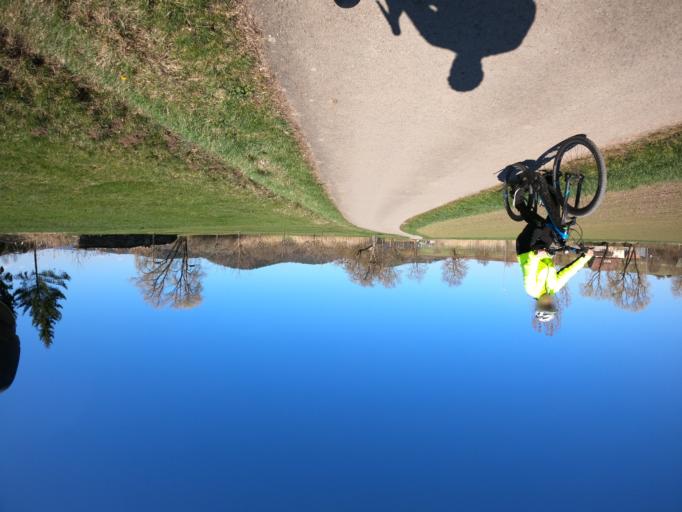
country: DE
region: Baden-Wuerttemberg
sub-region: Tuebingen Region
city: Rangendingen
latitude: 48.3864
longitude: 8.8769
